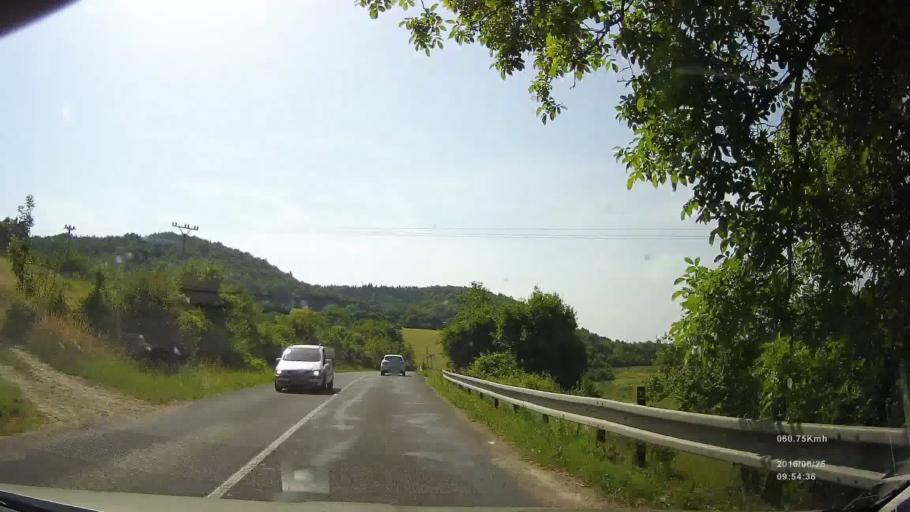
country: SK
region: Banskobystricky
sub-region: Okres Banska Bystrica
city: Banska Bystrica
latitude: 48.6941
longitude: 19.2172
